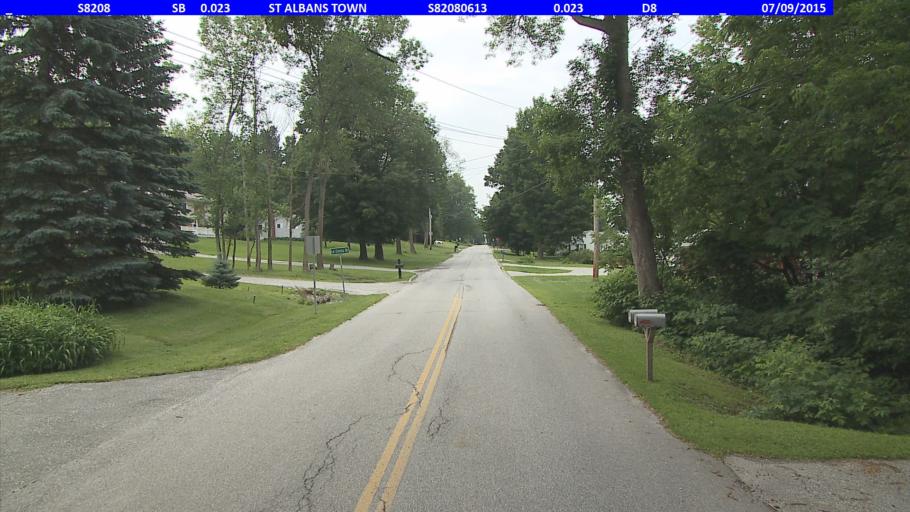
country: US
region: Vermont
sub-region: Franklin County
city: Saint Albans
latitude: 44.8244
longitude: -73.0761
